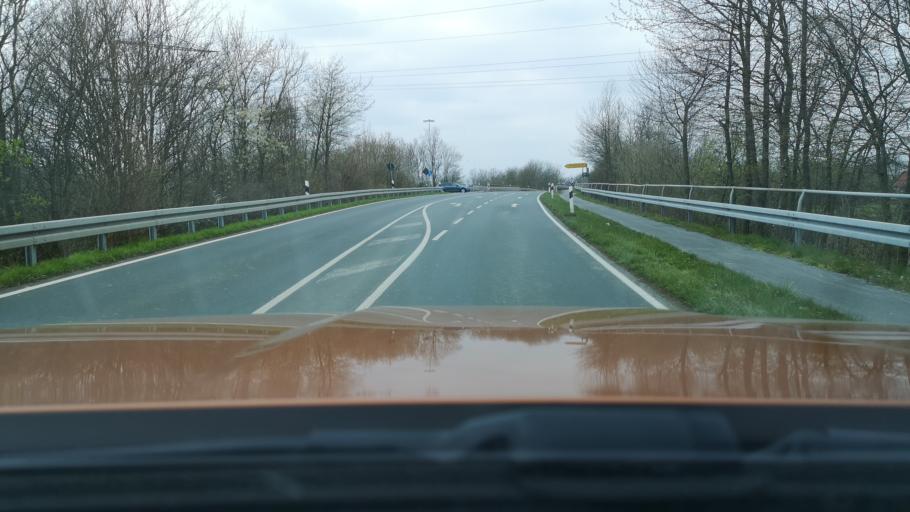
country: DE
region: Lower Saxony
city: Seggebruch
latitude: 52.2921
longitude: 9.0913
